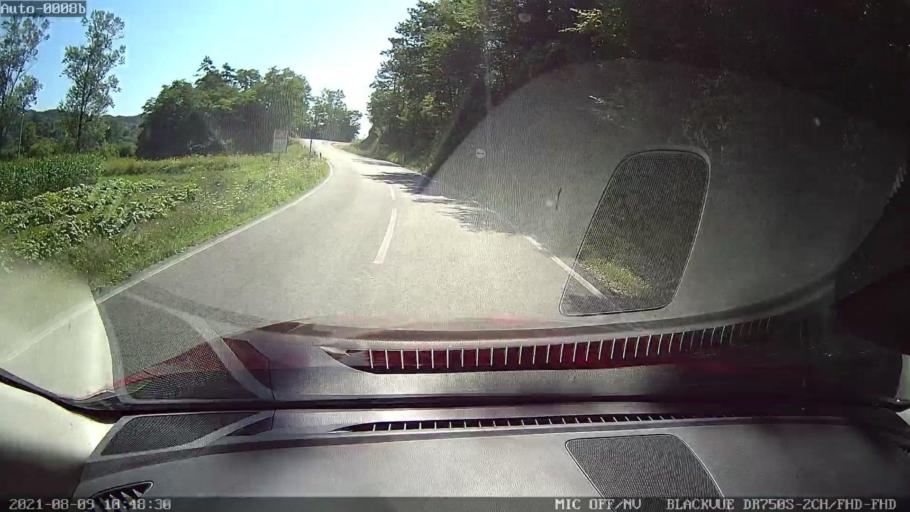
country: HR
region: Istarska
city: Pazin
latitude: 45.2709
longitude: 14.0242
